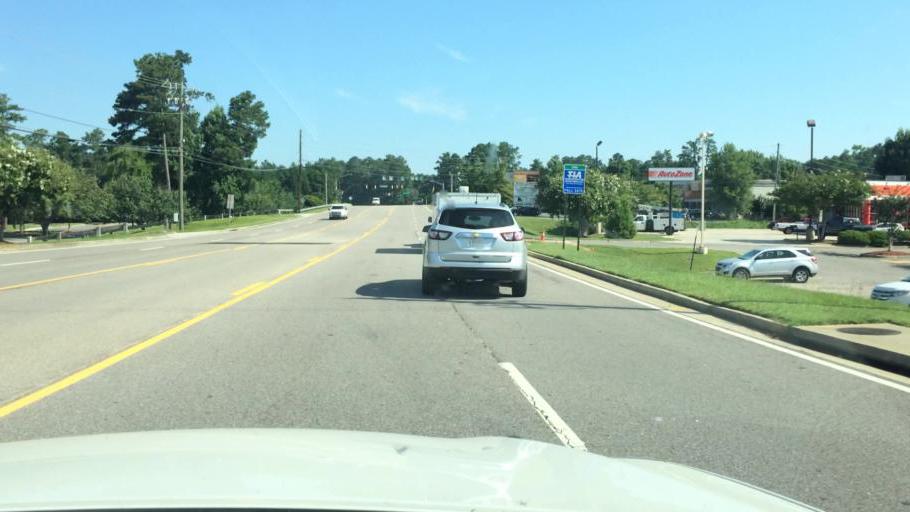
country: US
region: Georgia
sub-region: Columbia County
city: Martinez
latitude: 33.5160
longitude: -82.0597
